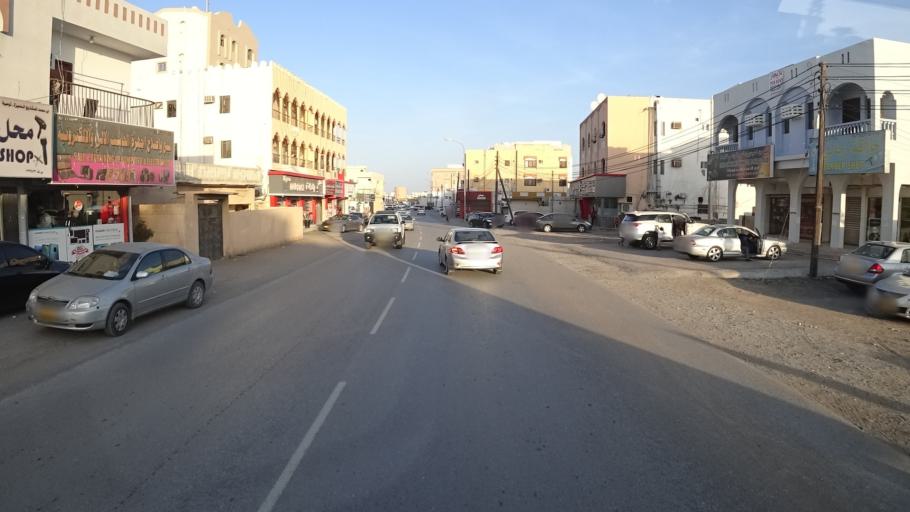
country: OM
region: Al Batinah
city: Barka'
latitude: 23.7071
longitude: 57.8900
